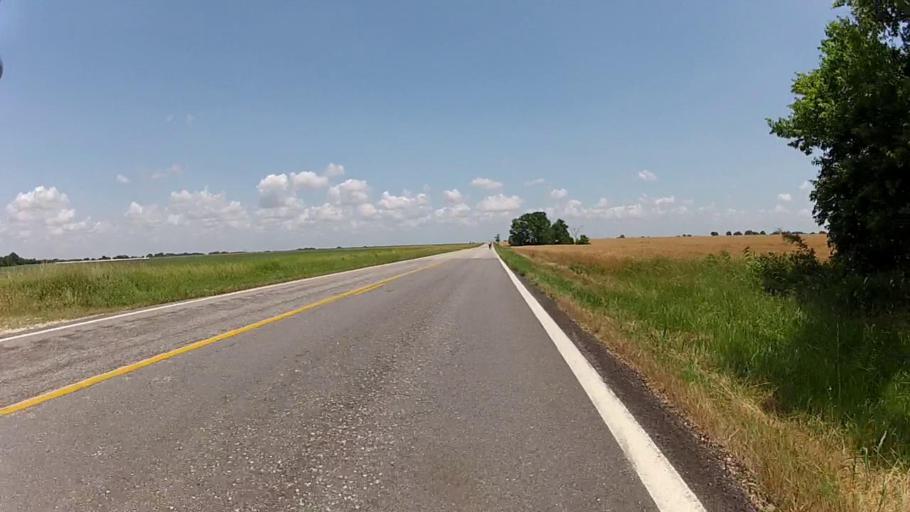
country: US
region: Kansas
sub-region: Montgomery County
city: Cherryvale
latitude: 37.1927
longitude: -95.4406
